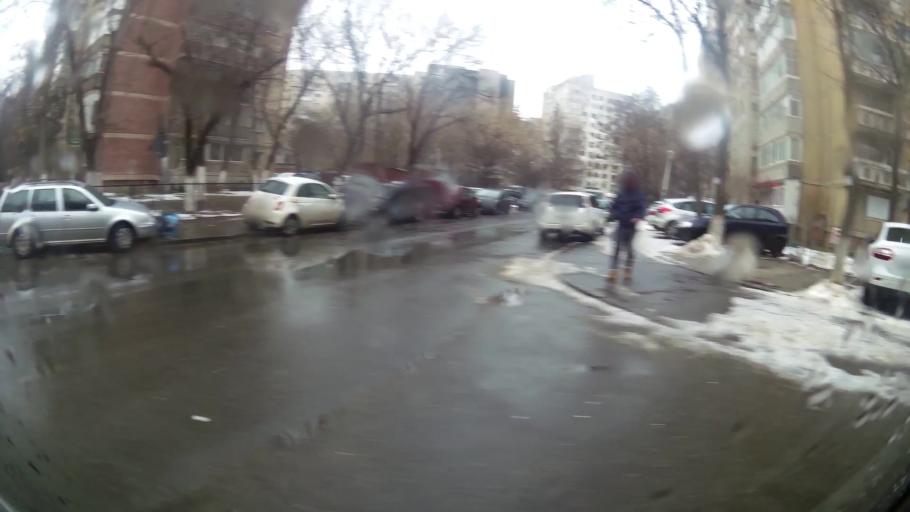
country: RO
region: Ilfov
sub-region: Comuna Chiajna
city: Rosu
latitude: 44.4325
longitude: 26.0100
